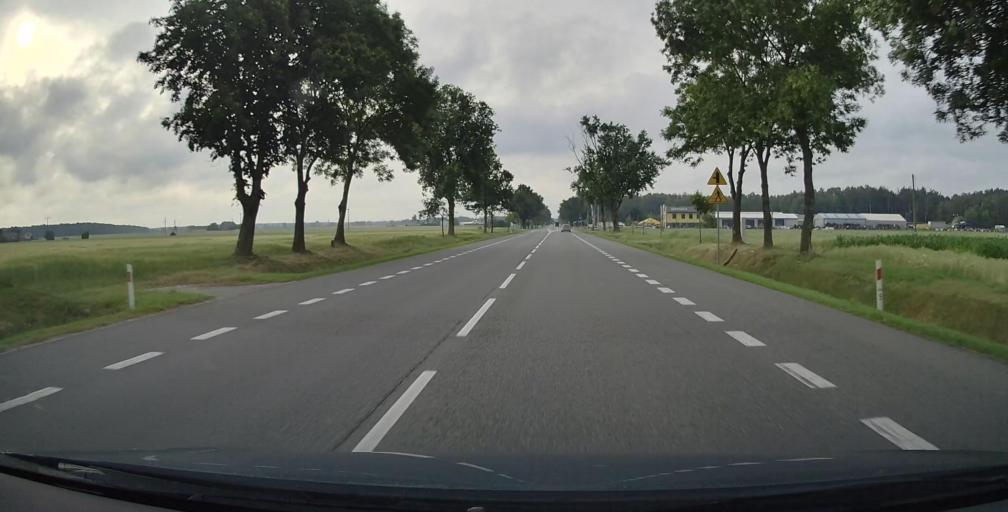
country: PL
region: Masovian Voivodeship
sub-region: Powiat siedlecki
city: Zbuczyn
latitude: 52.1011
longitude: 22.4035
